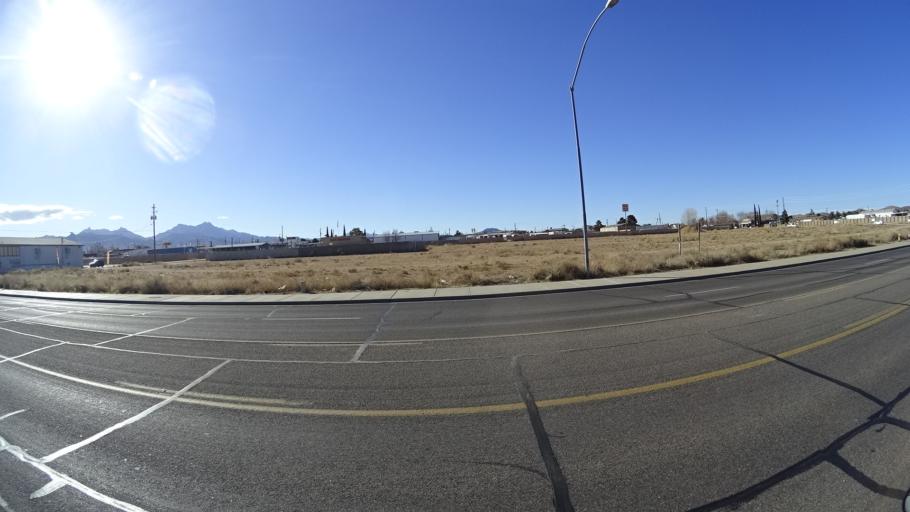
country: US
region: Arizona
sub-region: Mohave County
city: New Kingman-Butler
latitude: 35.2249
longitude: -114.0099
